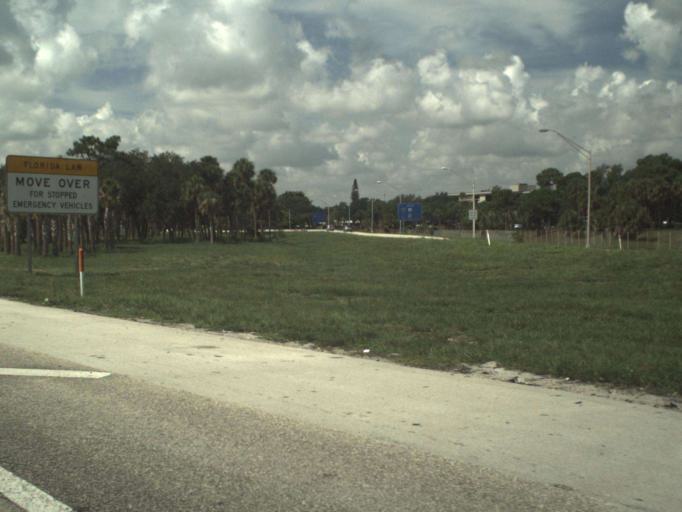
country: US
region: Florida
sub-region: Broward County
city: Deerfield Beach
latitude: 26.3224
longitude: -80.1167
